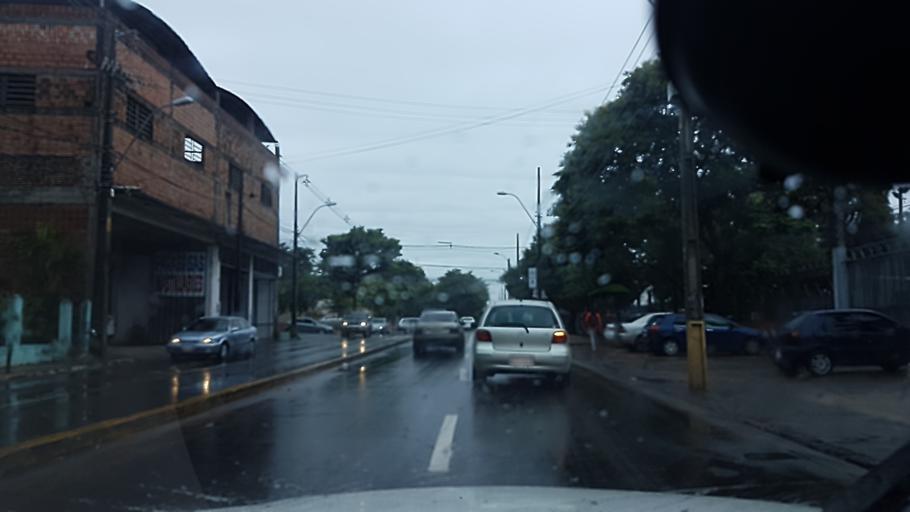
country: PY
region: Central
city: Lambare
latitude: -25.3160
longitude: -57.5736
